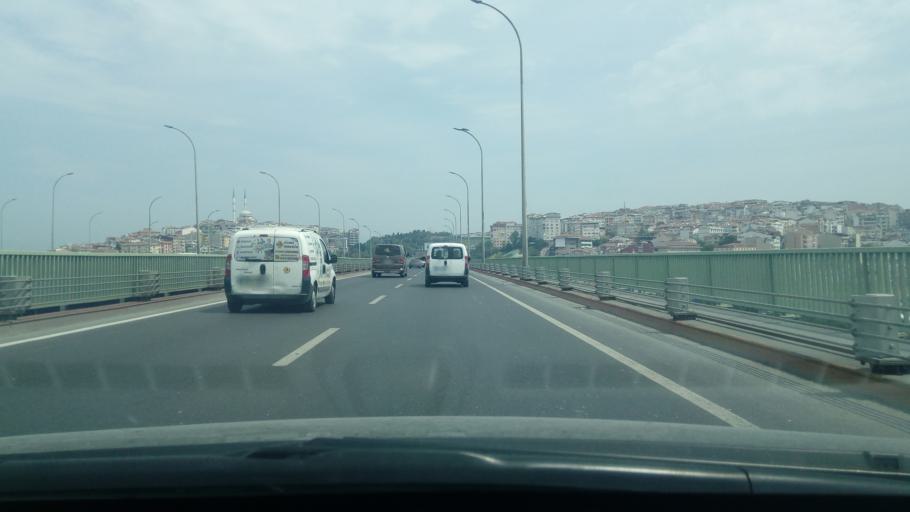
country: TR
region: Istanbul
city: Istanbul
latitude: 41.0408
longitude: 28.9400
